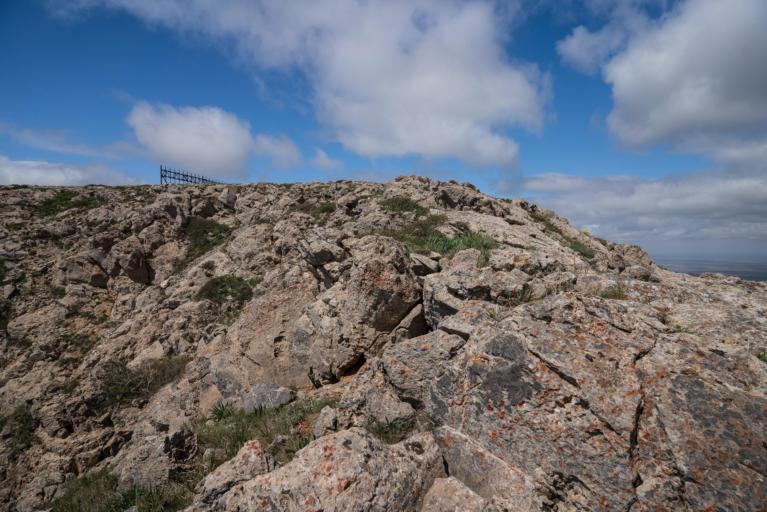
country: KZ
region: Ongtustik Qazaqstan
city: Ashchysay
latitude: 43.6410
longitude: 68.9254
